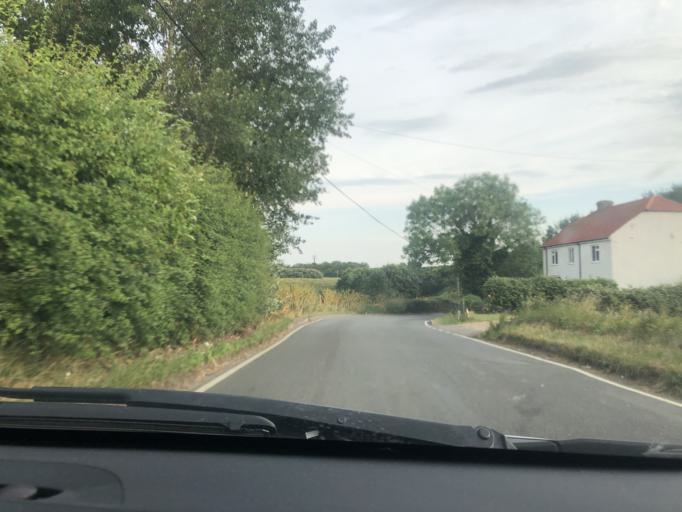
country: GB
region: England
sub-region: Kent
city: Herne Bay
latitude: 51.3650
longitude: 1.1728
